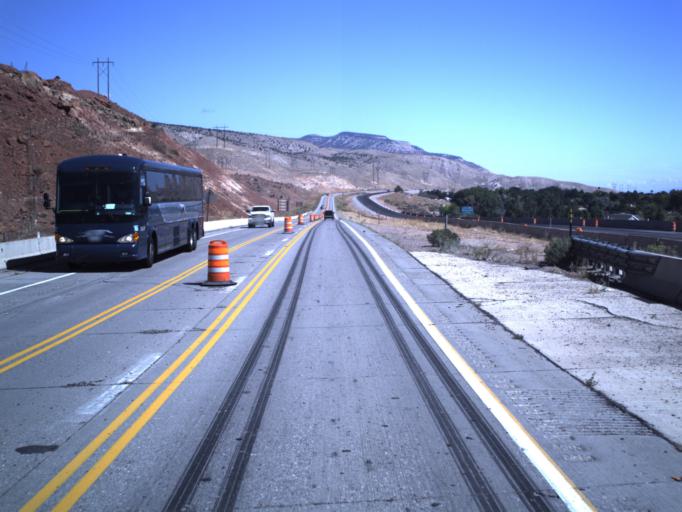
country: US
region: Utah
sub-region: Sevier County
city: Richfield
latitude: 38.7729
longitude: -112.0989
